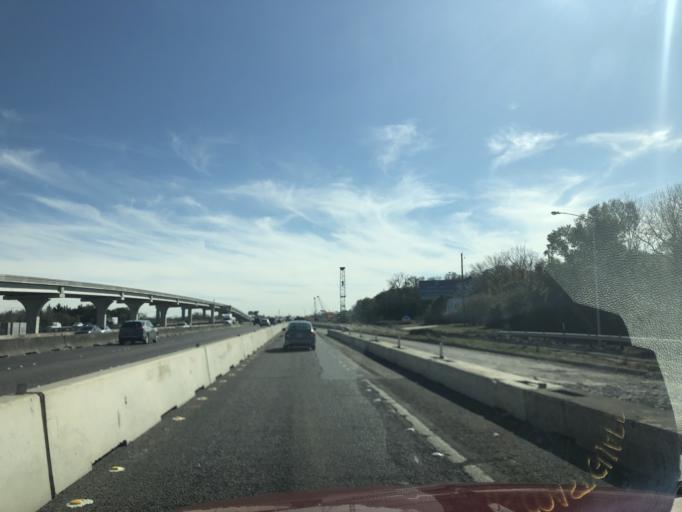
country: US
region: Texas
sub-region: Harris County
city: Webster
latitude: 29.5126
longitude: -95.1200
